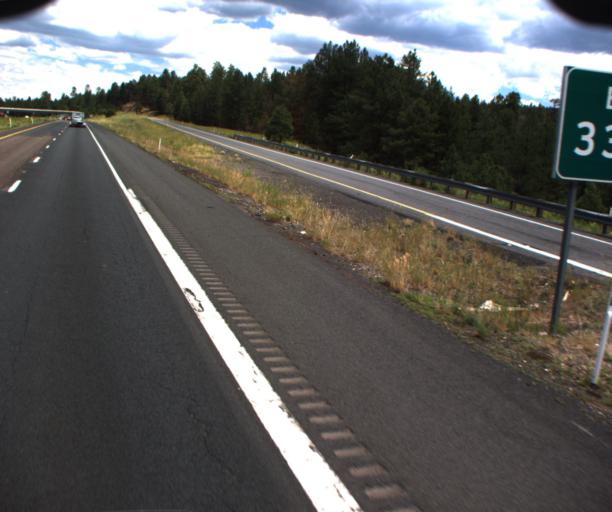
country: US
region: Arizona
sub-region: Coconino County
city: Mountainaire
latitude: 35.0472
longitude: -111.6840
